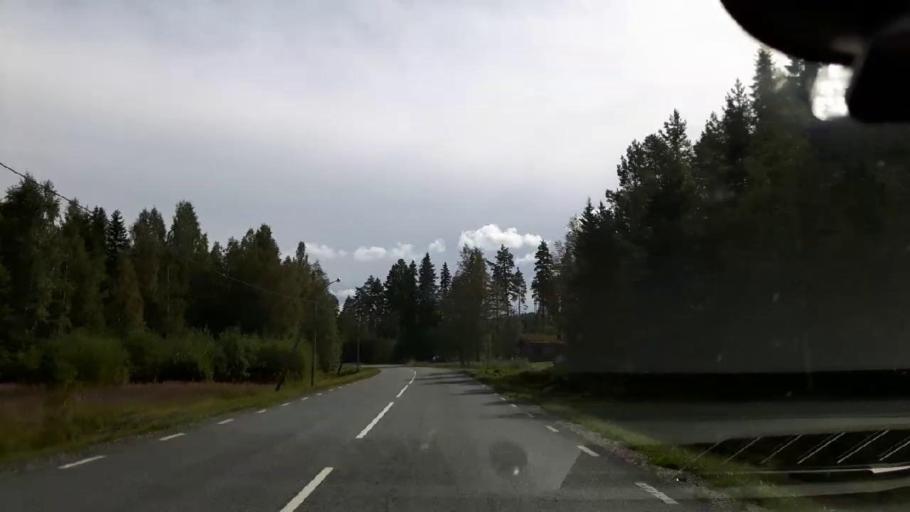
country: SE
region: Jaemtland
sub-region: Braecke Kommun
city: Braecke
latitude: 63.1557
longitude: 15.7128
